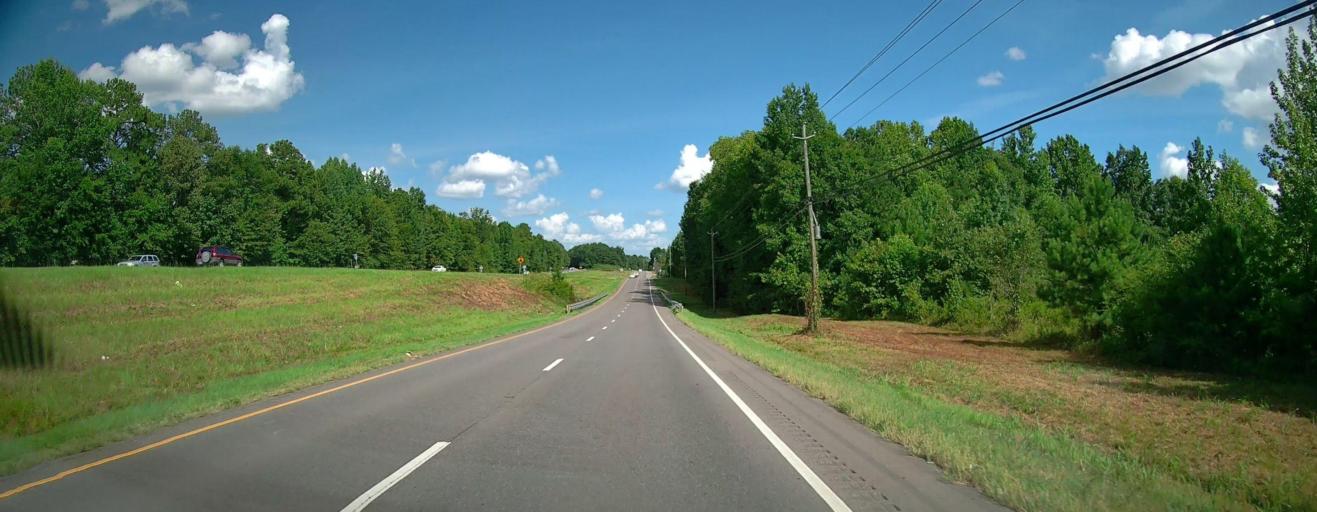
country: US
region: Alabama
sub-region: Tuscaloosa County
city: Northport
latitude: 33.2404
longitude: -87.6622
